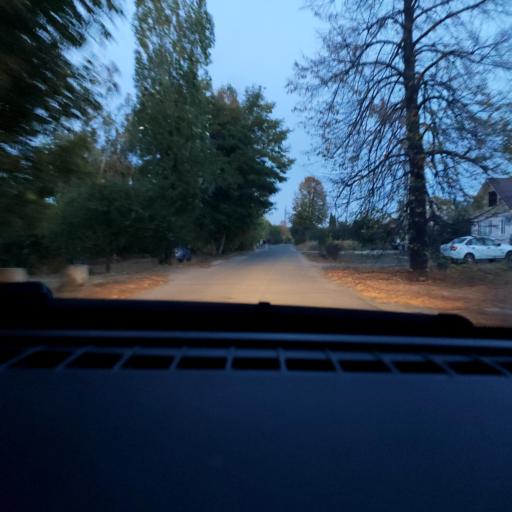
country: RU
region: Voronezj
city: Maslovka
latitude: 51.6155
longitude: 39.2682
